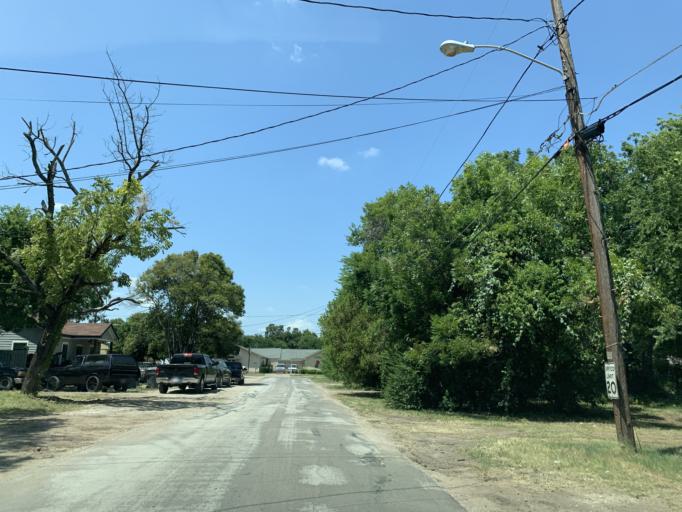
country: US
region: Texas
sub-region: Dallas County
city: Hutchins
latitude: 32.6860
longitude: -96.7823
